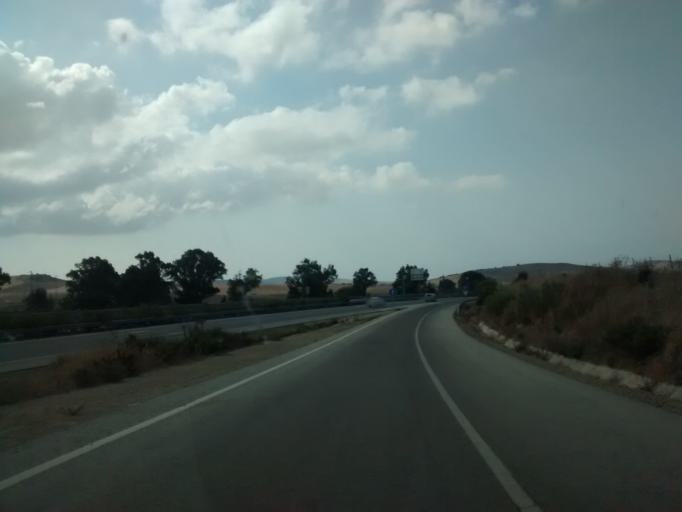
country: ES
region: Andalusia
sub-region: Provincia de Cadiz
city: Conil de la Frontera
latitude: 36.2694
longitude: -6.0283
